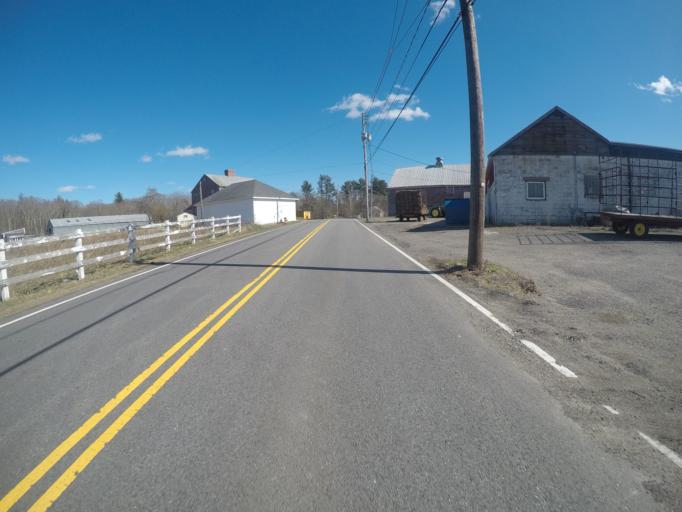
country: US
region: Massachusetts
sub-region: Bristol County
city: Easton
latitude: 42.0389
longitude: -71.1383
